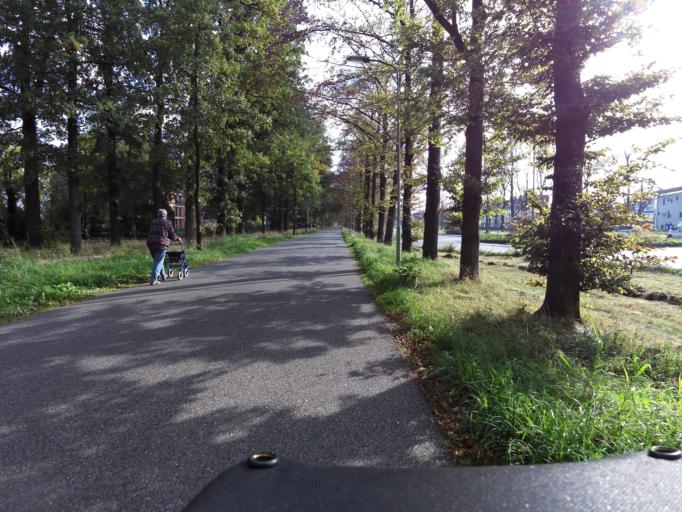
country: NL
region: Gelderland
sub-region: Gemeente Wageningen
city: Wageningen
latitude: 51.9742
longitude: 5.6518
